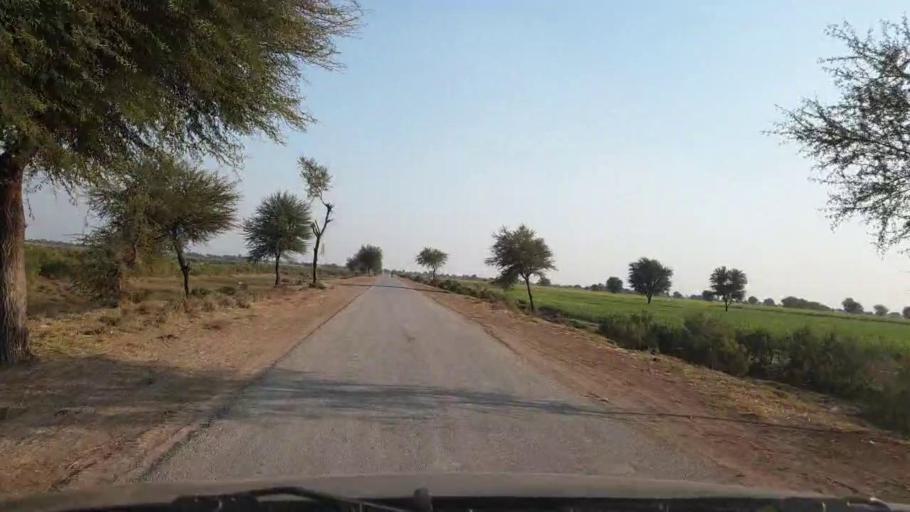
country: PK
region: Sindh
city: Jhol
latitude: 25.9393
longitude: 68.9112
